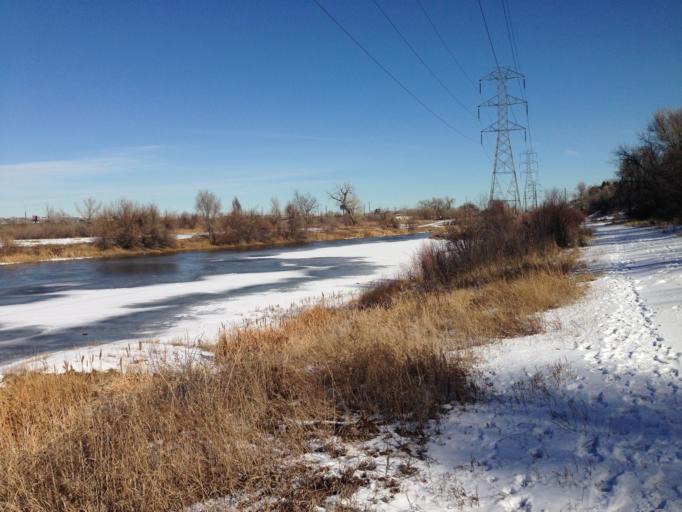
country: US
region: Colorado
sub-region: Adams County
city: Berkley
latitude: 39.7954
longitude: -105.0381
